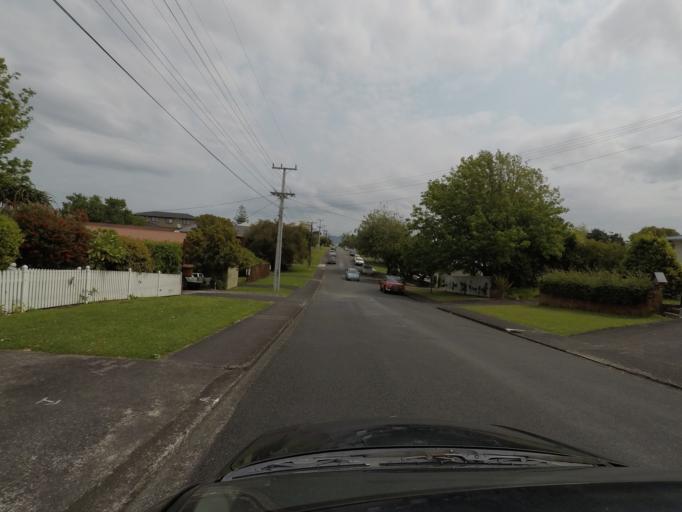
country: NZ
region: Auckland
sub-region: Auckland
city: Rosebank
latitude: -36.8398
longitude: 174.6403
